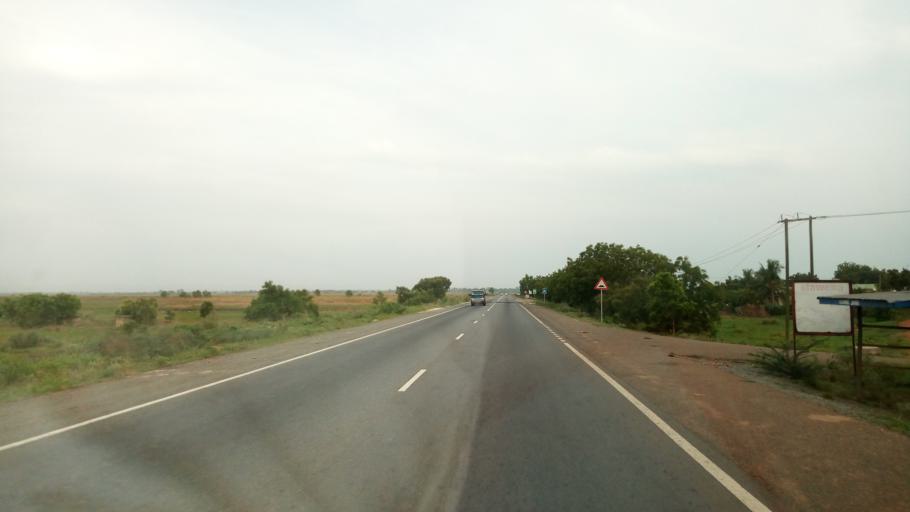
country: GH
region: Volta
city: Keta
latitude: 6.0541
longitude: 0.9652
